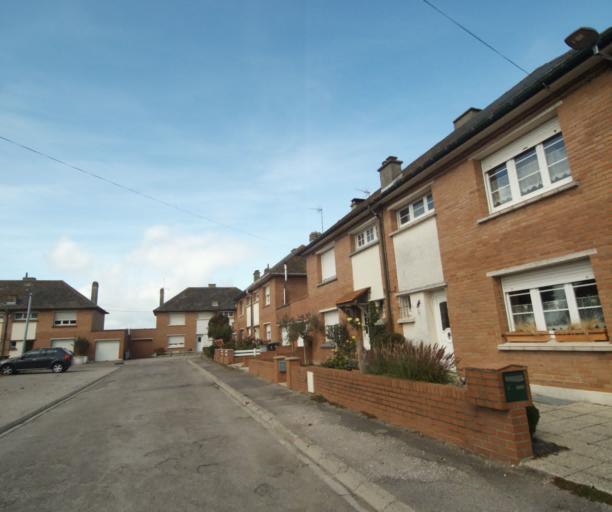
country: FR
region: Nord-Pas-de-Calais
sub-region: Departement du Pas-de-Calais
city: Etaples
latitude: 50.5250
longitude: 1.6262
